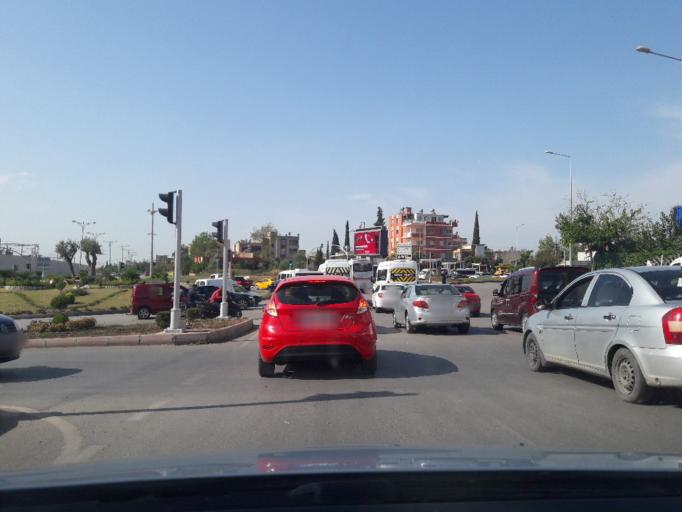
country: TR
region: Adana
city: Adana
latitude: 37.0035
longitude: 35.3128
